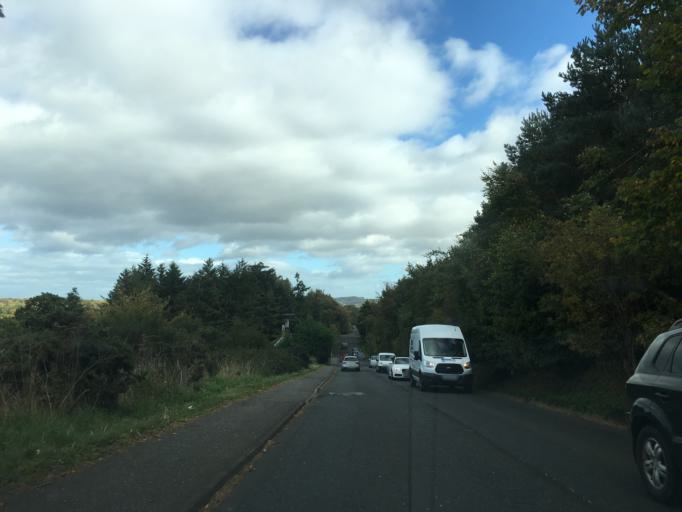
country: GB
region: Scotland
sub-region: Midlothian
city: Bonnyrigg
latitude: 55.8863
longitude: -3.1039
